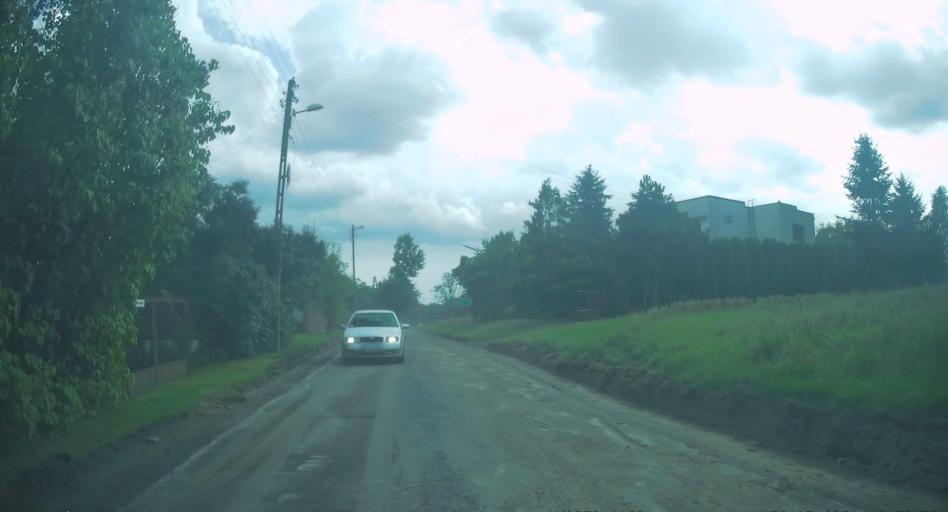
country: PL
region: Lodz Voivodeship
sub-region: Powiat brzezinski
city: Rogow
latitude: 51.8075
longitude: 19.8952
